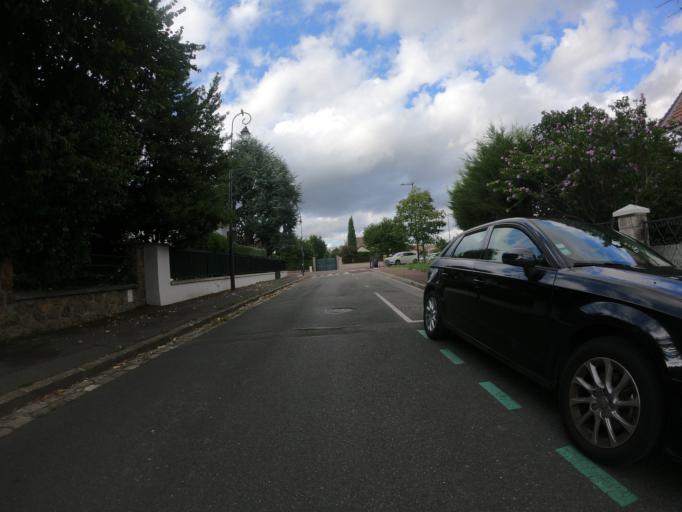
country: FR
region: Ile-de-France
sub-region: Departement des Hauts-de-Seine
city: Antony
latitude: 48.7576
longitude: 2.2869
